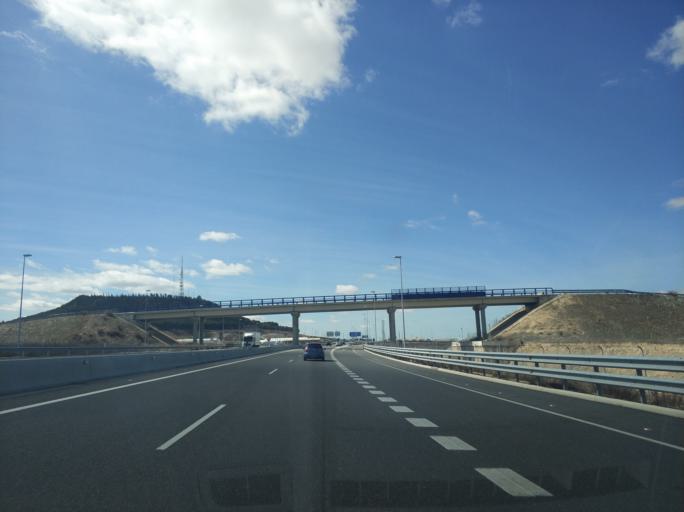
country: ES
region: Castille and Leon
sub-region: Provincia de Valladolid
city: Cisterniga
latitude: 41.6236
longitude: -4.6889
